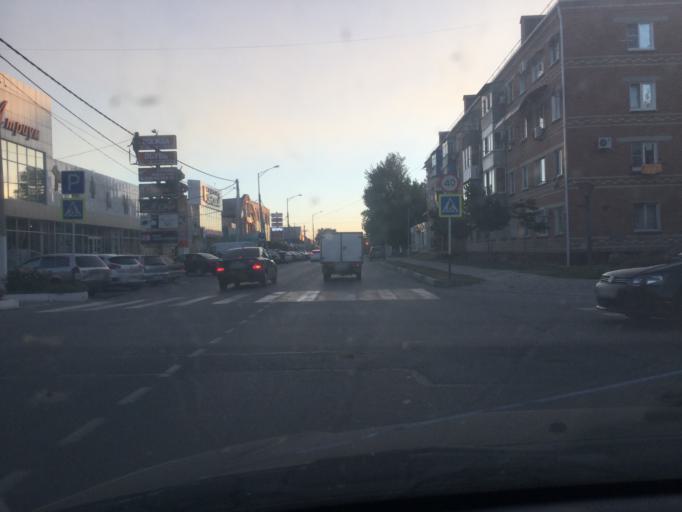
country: RU
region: Krasnodarskiy
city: Slavyansk-na-Kubani
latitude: 45.2548
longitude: 38.1193
